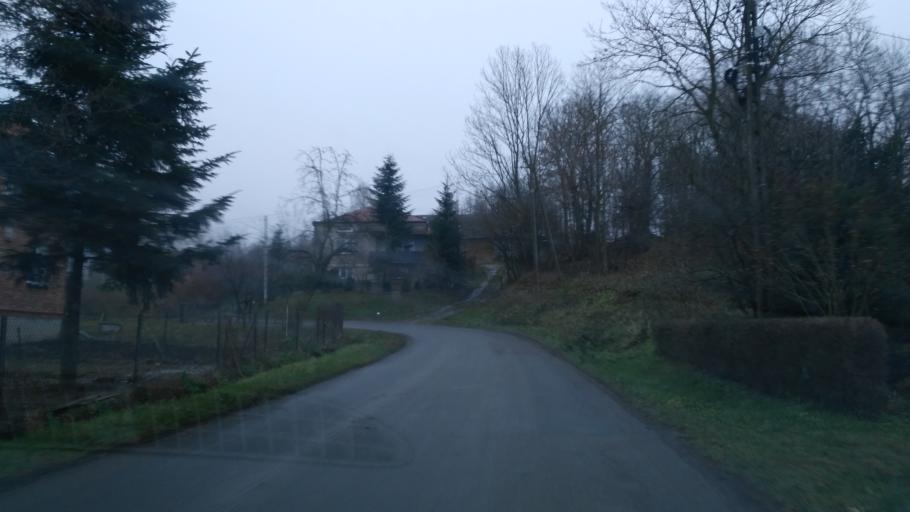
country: PL
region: Subcarpathian Voivodeship
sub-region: Powiat przeworski
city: Zarzecze
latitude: 49.9688
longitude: 22.5676
